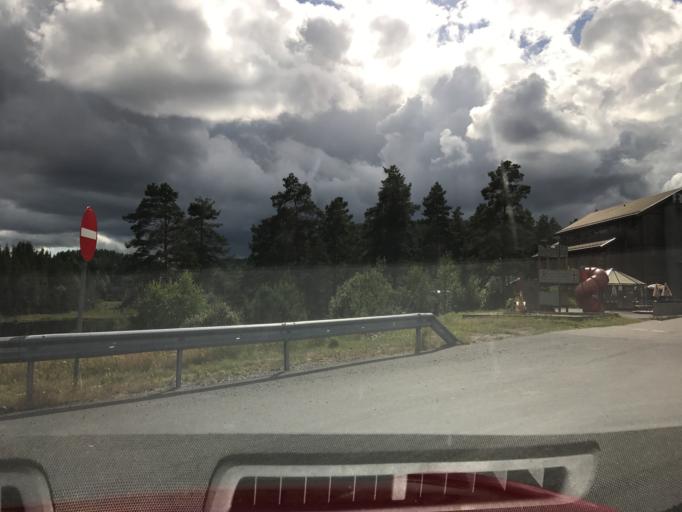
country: NO
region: Aust-Agder
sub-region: Gjerstad
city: Gjerstad
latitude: 58.8204
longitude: 9.0743
